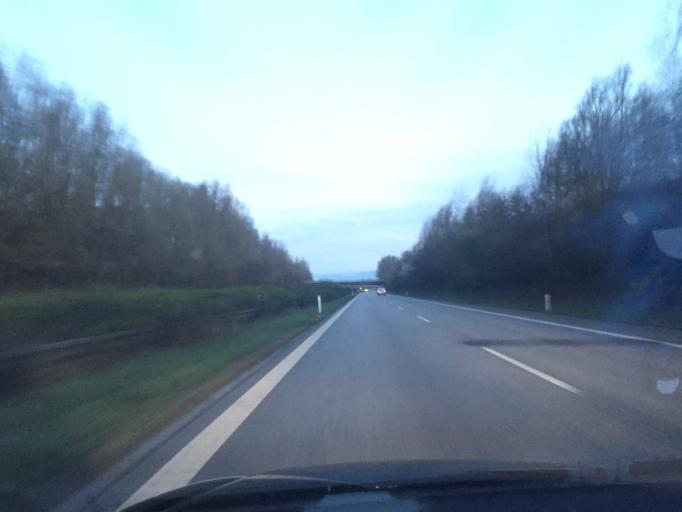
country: DK
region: Capital Region
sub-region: Fredensborg Kommune
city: Niva
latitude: 55.9397
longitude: 12.4788
